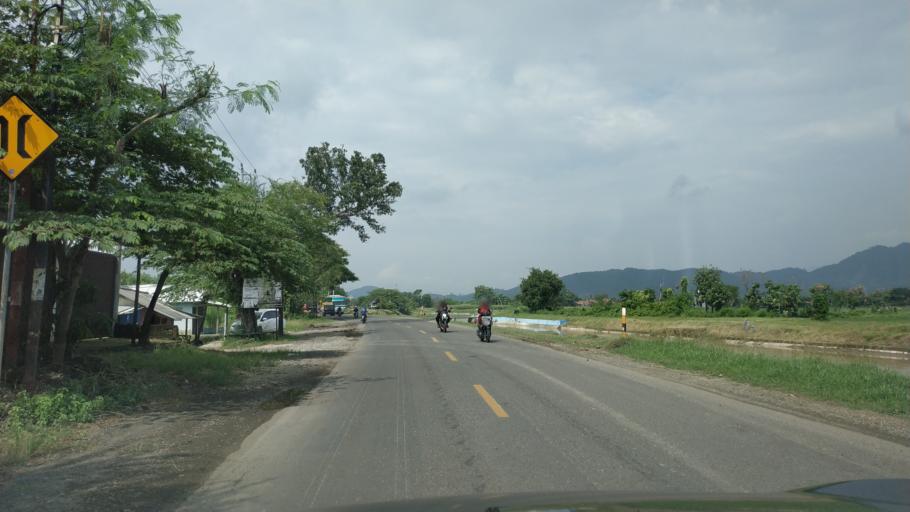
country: ID
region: Central Java
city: Margasari
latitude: -7.0874
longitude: 108.9838
